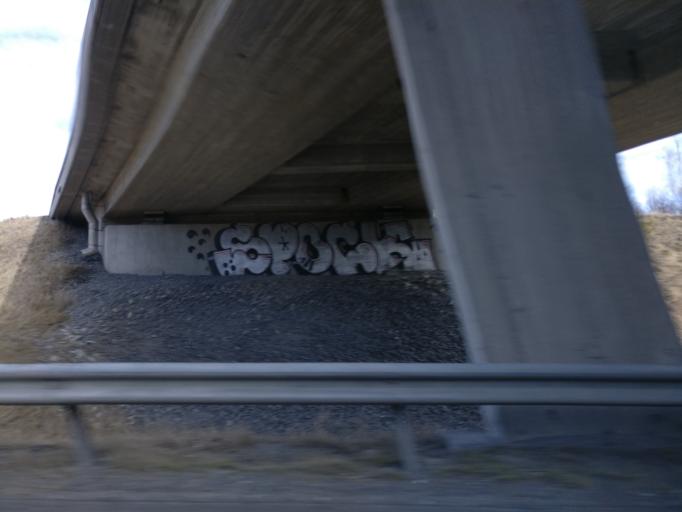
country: FI
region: Pirkanmaa
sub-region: Tampere
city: Lempaeaelae
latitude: 61.3963
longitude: 23.7835
